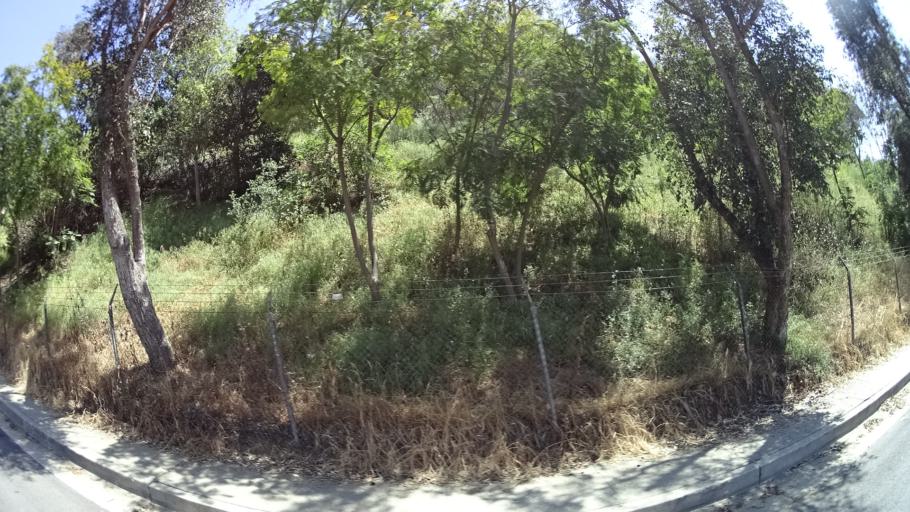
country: US
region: California
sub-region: Los Angeles County
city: Echo Park
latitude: 34.0740
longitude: -118.2469
